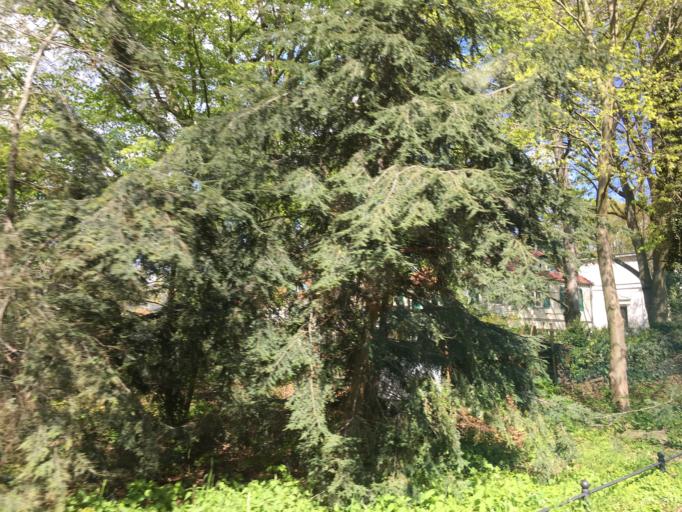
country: DE
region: Brandenburg
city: Potsdam
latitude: 52.4169
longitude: 13.0673
